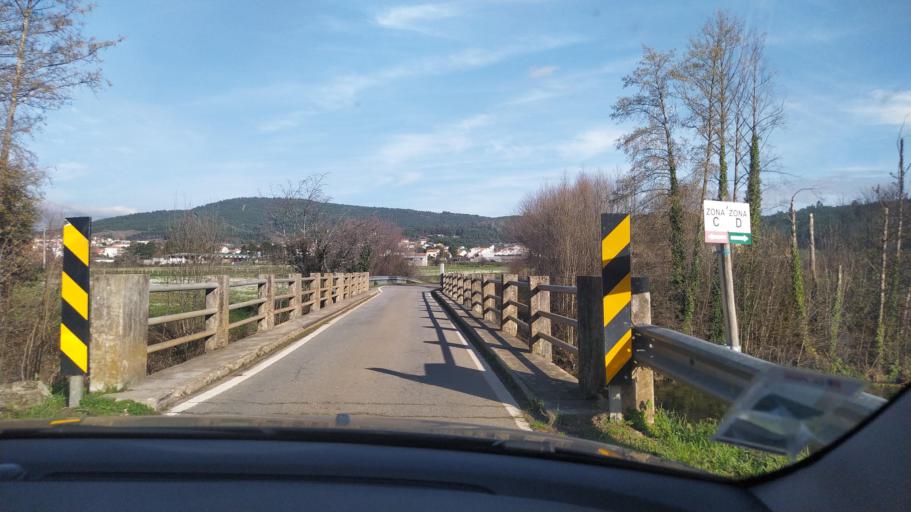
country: PT
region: Castelo Branco
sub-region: Concelho do Fundao
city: Aldeia de Joanes
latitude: 40.1880
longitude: -7.6428
